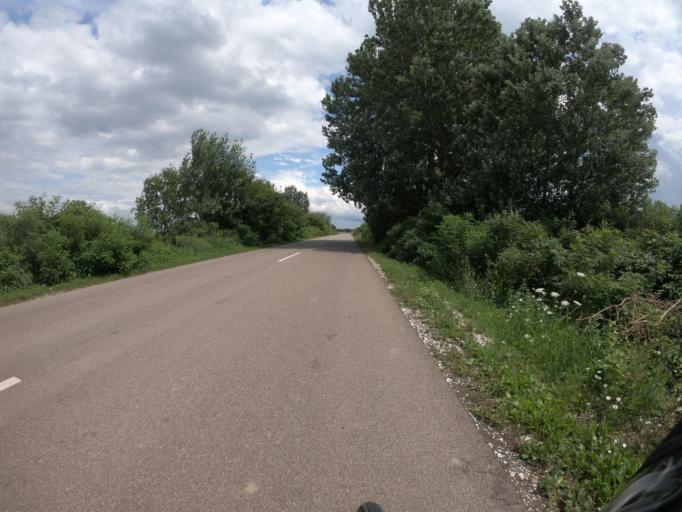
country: HU
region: Jasz-Nagykun-Szolnok
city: Tiszafured
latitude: 47.6908
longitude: 20.7883
